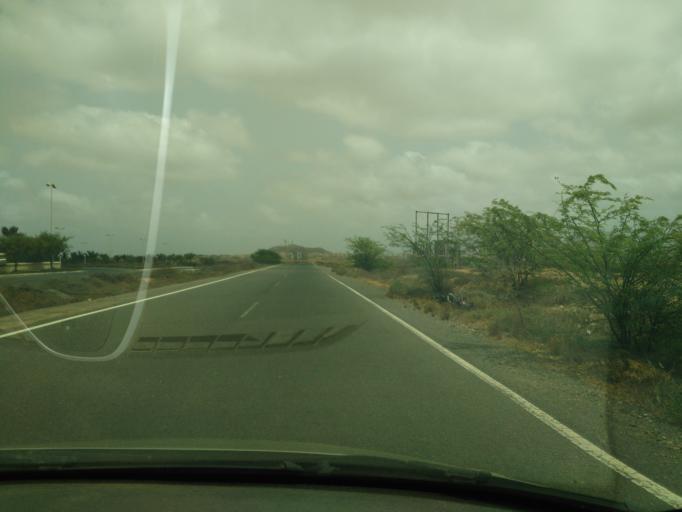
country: CV
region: Sal
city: Espargos
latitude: 16.7332
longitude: -22.9417
